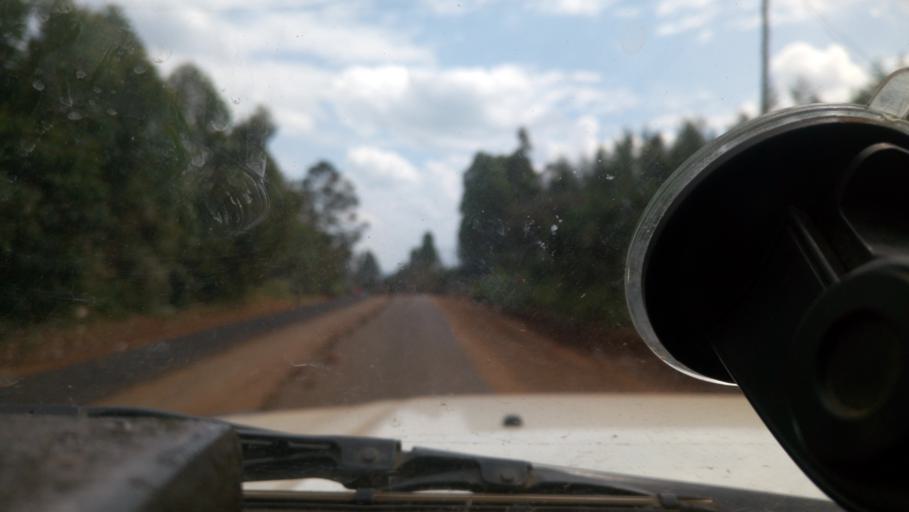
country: KE
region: Kericho
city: Litein
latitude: -0.5792
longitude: 35.1432
